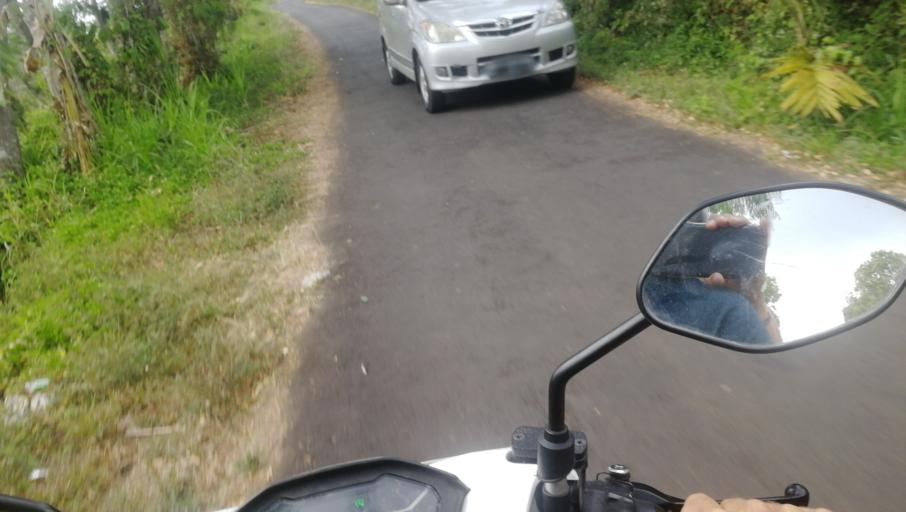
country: ID
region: Bali
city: Banjar Ambengan
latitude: -8.2146
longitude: 115.1098
